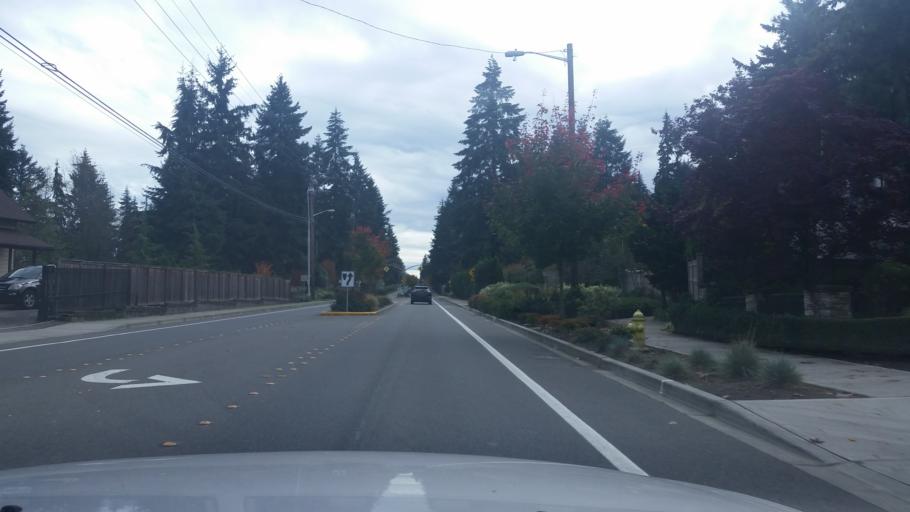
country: US
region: Washington
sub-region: King County
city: Eastgate
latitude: 47.5943
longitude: -122.1488
